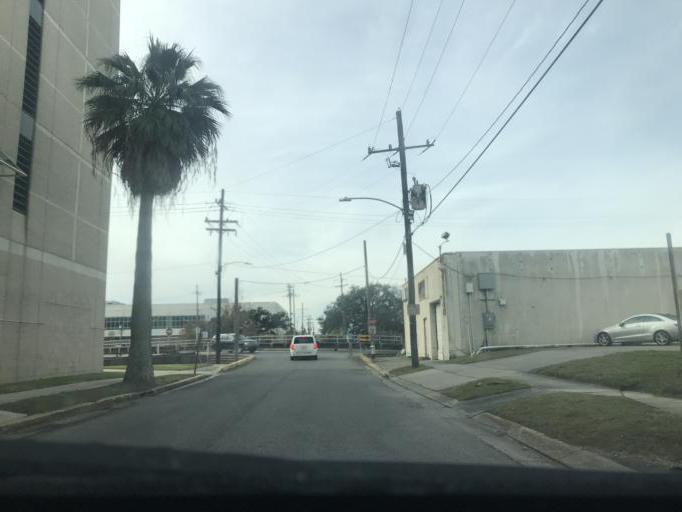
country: US
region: Louisiana
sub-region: Orleans Parish
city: New Orleans
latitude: 29.9656
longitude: -90.1085
